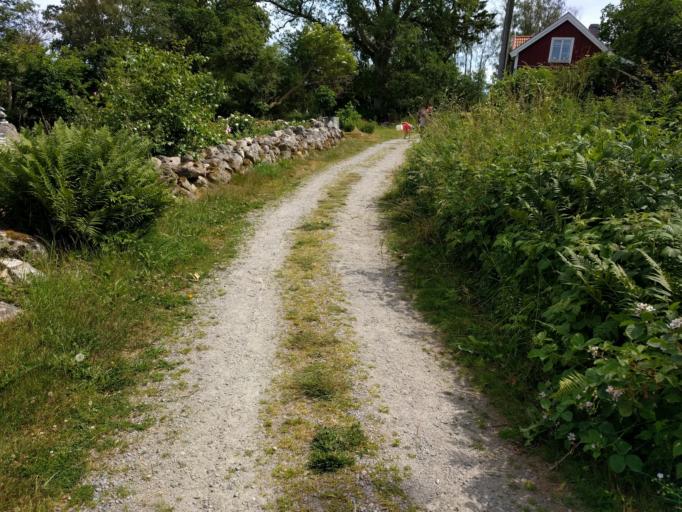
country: SE
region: Blekinge
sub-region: Karlshamns Kommun
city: Karlshamn
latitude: 56.1191
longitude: 14.9707
